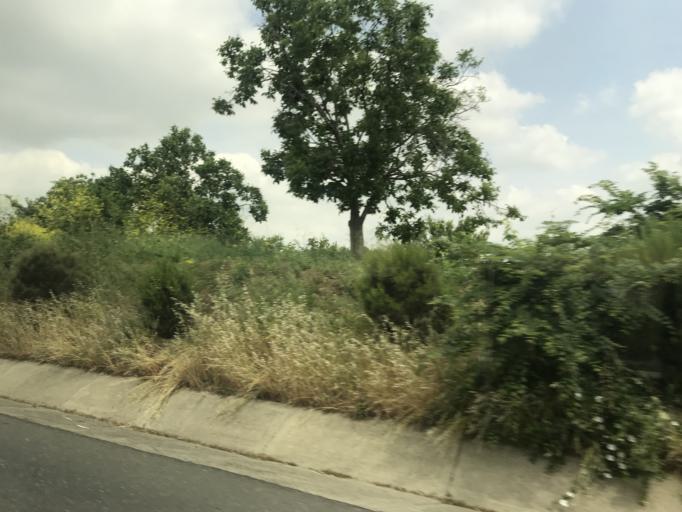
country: TR
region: Tekirdag
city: Tekirdag
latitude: 41.0010
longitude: 27.5475
